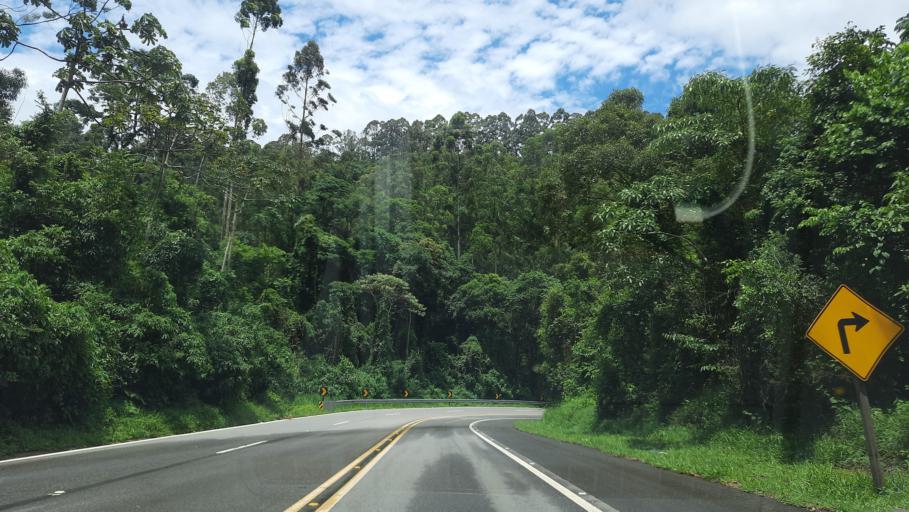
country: BR
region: Minas Gerais
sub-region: Pocos De Caldas
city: Pocos de Caldas
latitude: -21.8429
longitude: -46.6940
